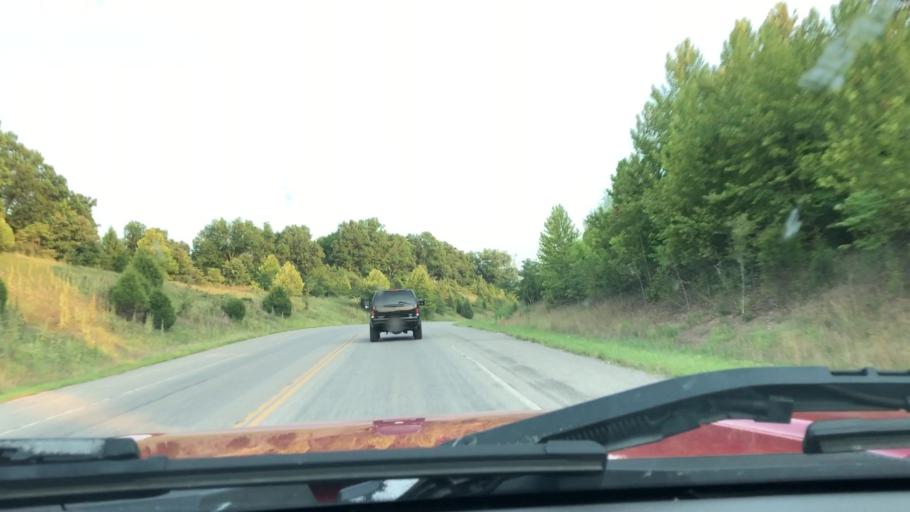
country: US
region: Missouri
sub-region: Jasper County
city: Joplin
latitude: 37.0246
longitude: -94.5143
